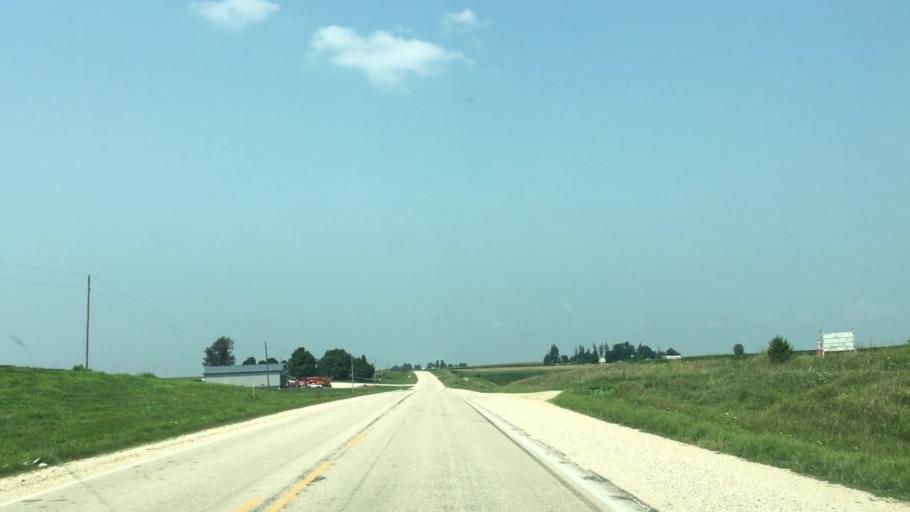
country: US
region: Iowa
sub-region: Fayette County
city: West Union
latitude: 42.9885
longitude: -91.8241
